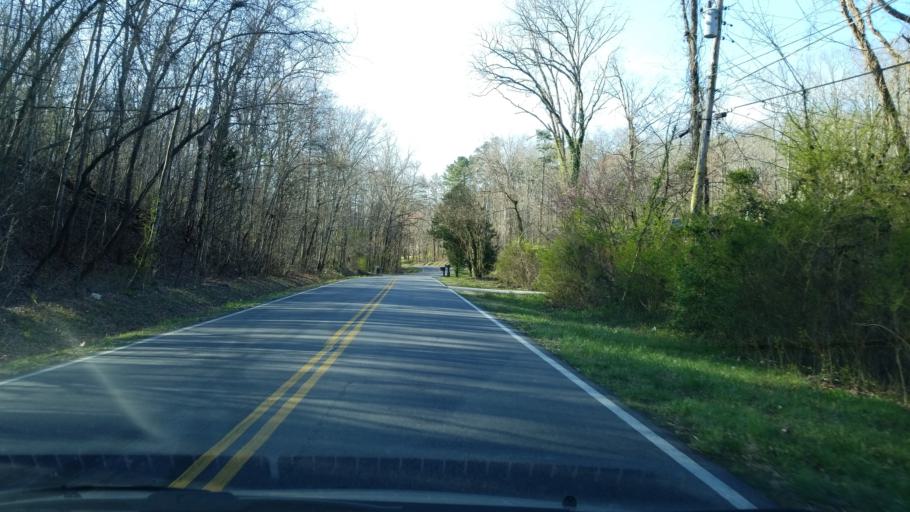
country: US
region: Tennessee
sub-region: Hamilton County
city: East Brainerd
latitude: 35.0200
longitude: -85.1137
